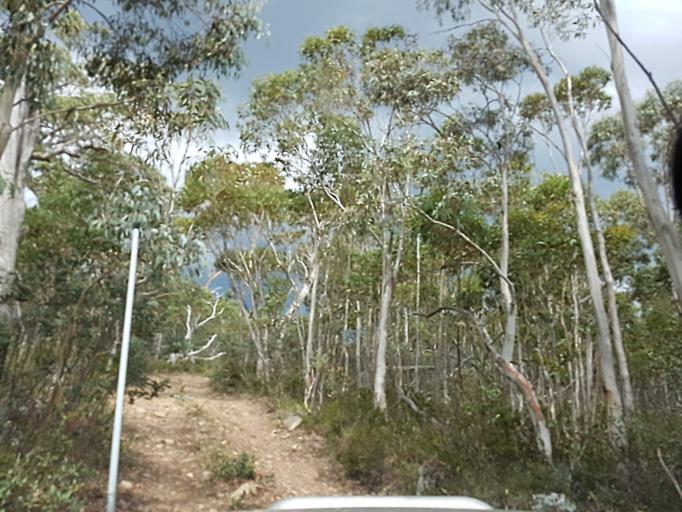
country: AU
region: New South Wales
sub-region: Snowy River
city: Jindabyne
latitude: -36.8776
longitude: 148.1796
